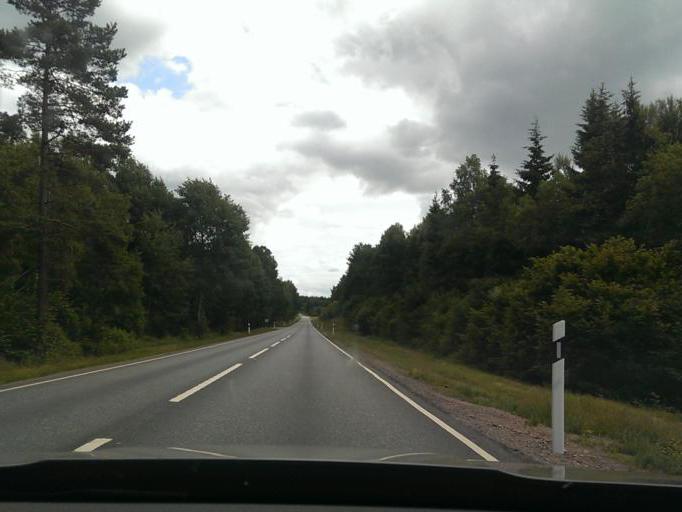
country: SE
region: Joenkoeping
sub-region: Varnamo Kommun
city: Varnamo
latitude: 57.2242
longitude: 14.0094
